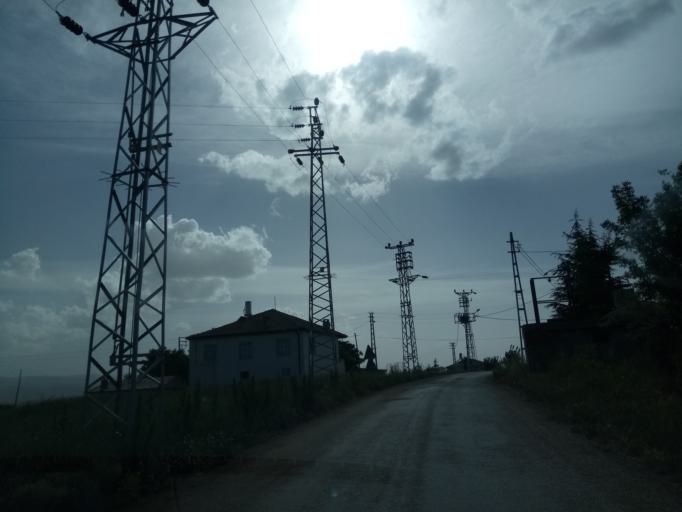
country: TR
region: Konya
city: Ahirli
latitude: 37.2843
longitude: 32.1788
